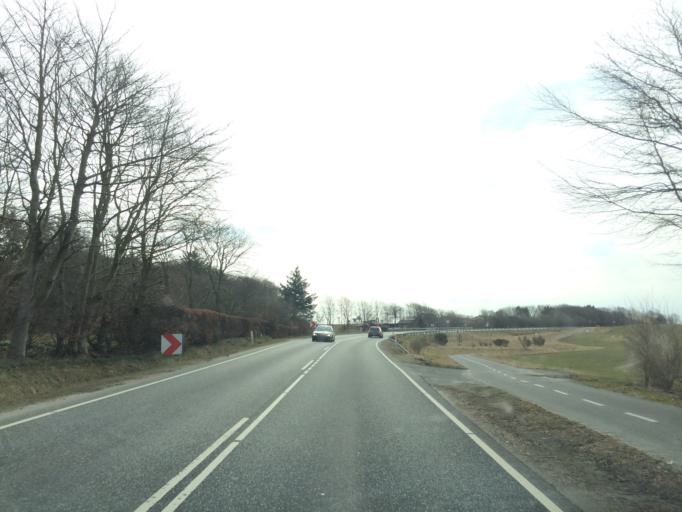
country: DK
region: Central Jutland
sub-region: Ringkobing-Skjern Kommune
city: Videbaek
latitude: 56.1083
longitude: 8.5065
